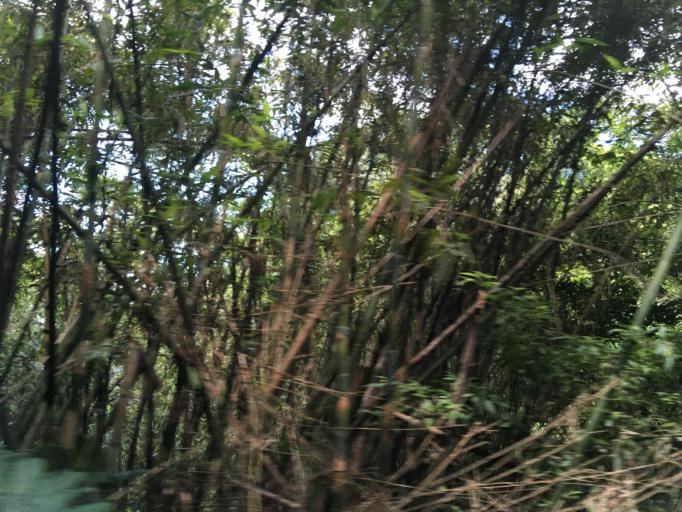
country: TW
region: Taipei
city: Taipei
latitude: 24.9389
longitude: 121.5764
